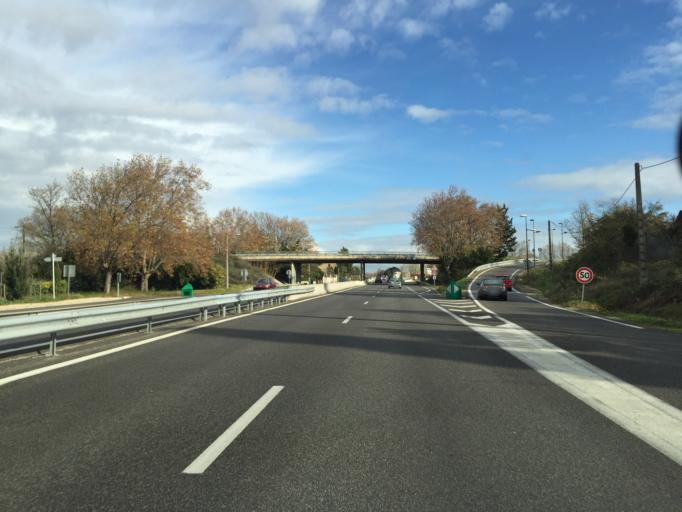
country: FR
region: Provence-Alpes-Cote d'Azur
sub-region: Departement du Vaucluse
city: Vedene
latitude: 43.9870
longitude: 4.8937
